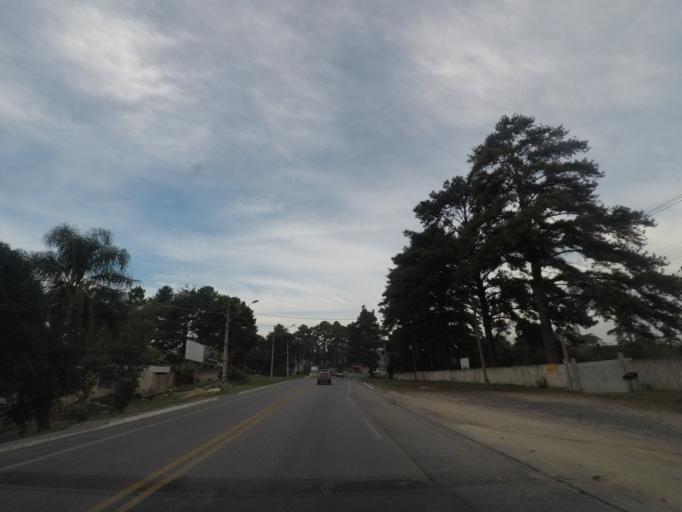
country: BR
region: Parana
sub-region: Curitiba
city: Curitiba
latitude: -25.3710
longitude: -49.2200
